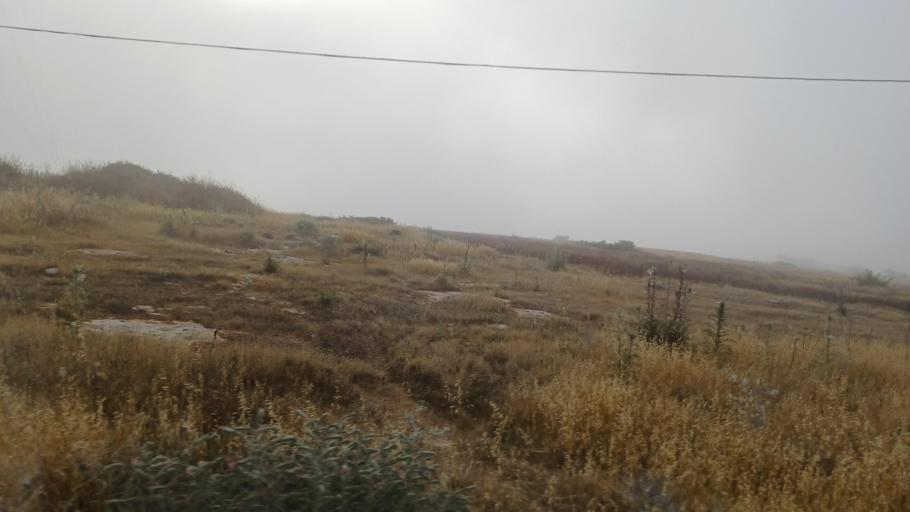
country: CY
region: Ammochostos
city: Acheritou
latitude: 35.1002
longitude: 33.8769
